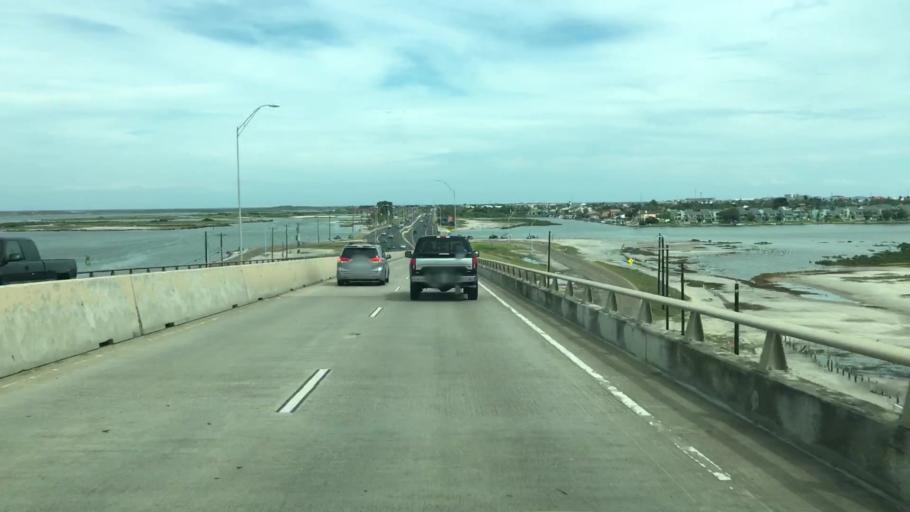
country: US
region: Texas
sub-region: Nueces County
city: Corpus Christi
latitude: 27.6336
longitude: -97.2373
